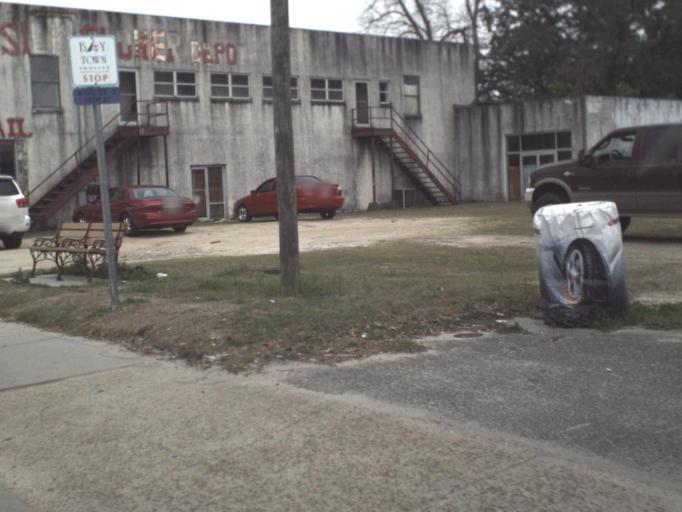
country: US
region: Florida
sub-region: Bay County
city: Springfield
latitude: 30.1568
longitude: -85.6245
